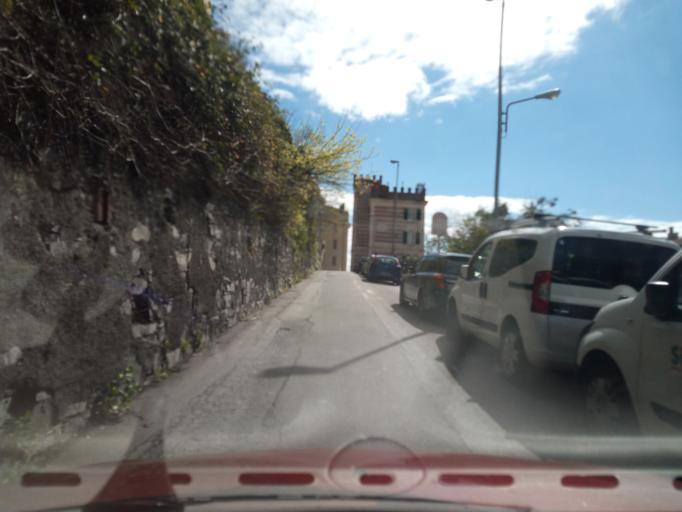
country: IT
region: Liguria
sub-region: Provincia di Genova
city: Genoa
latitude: 44.4189
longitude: 8.9193
